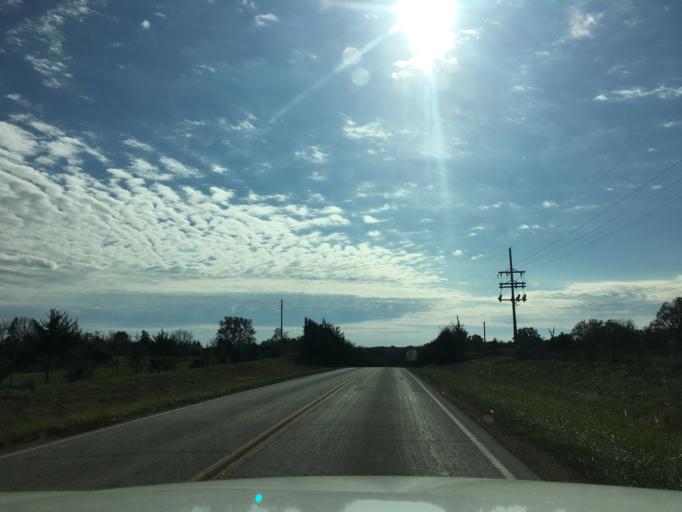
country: US
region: Missouri
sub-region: Osage County
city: Linn
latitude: 38.4017
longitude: -91.8198
